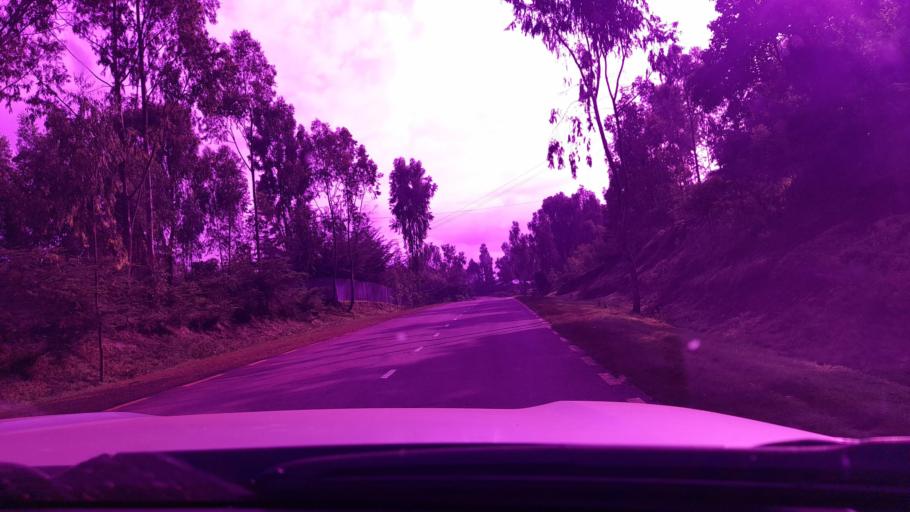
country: ET
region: Oromiya
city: Bedele
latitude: 8.2187
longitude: 36.4452
